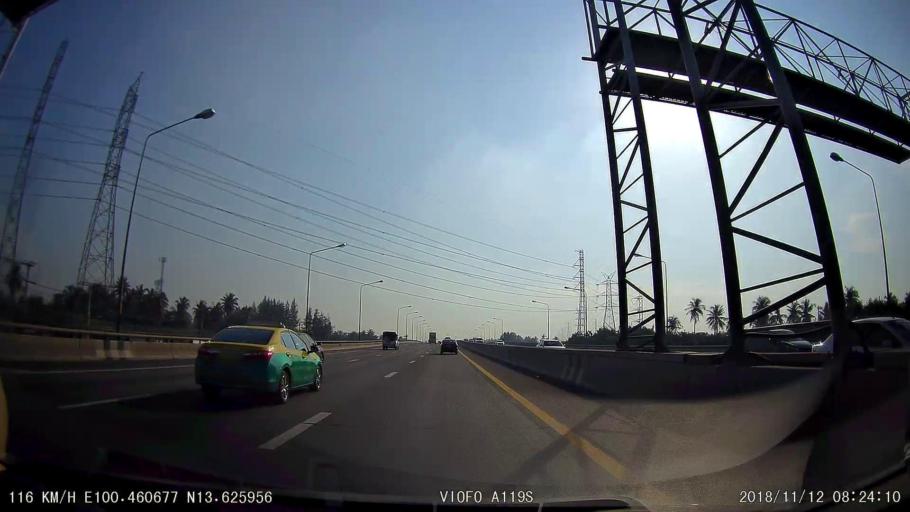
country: TH
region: Bangkok
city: Bang Khun Thian
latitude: 13.6259
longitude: 100.4613
